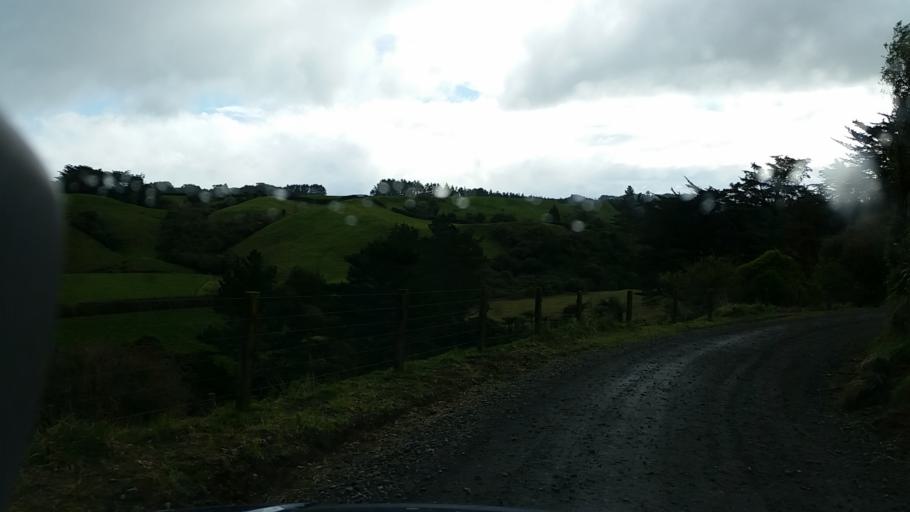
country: NZ
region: Taranaki
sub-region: South Taranaki District
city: Eltham
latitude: -39.2816
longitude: 174.3351
